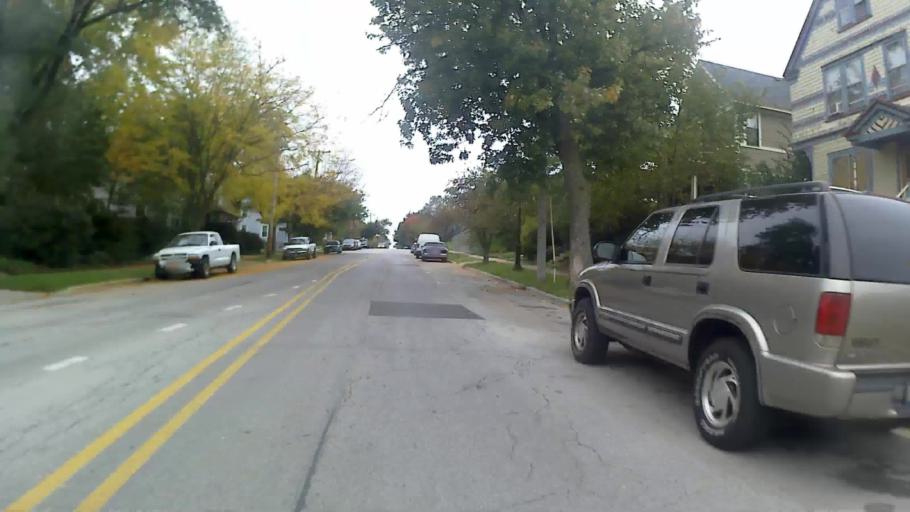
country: US
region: Illinois
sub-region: Kane County
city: Aurora
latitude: 41.7593
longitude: -88.3200
